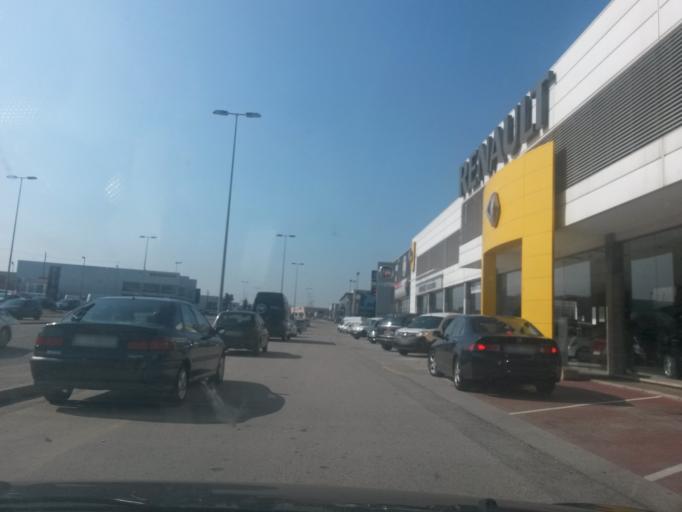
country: ES
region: Catalonia
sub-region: Provincia de Girona
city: Fornells de la Selva
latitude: 41.9366
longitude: 2.7991
